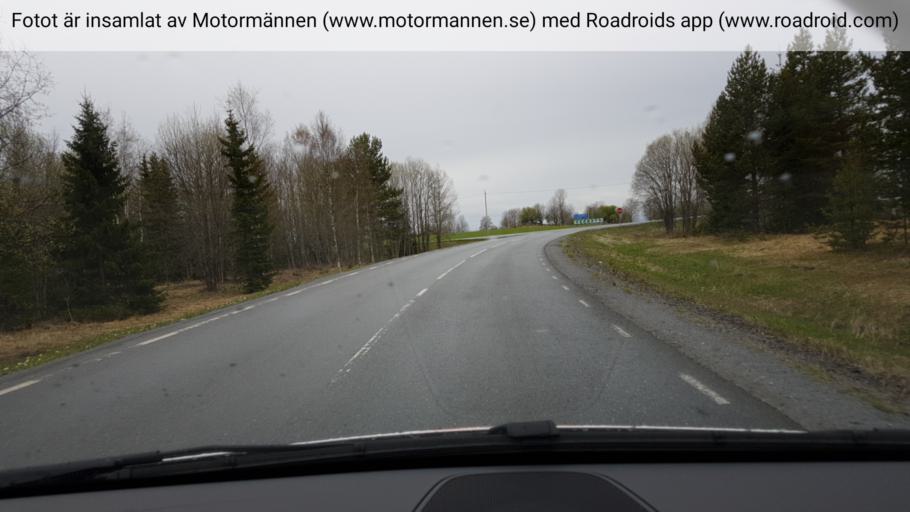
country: SE
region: Jaemtland
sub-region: Krokoms Kommun
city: Krokom
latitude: 63.2486
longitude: 14.4256
